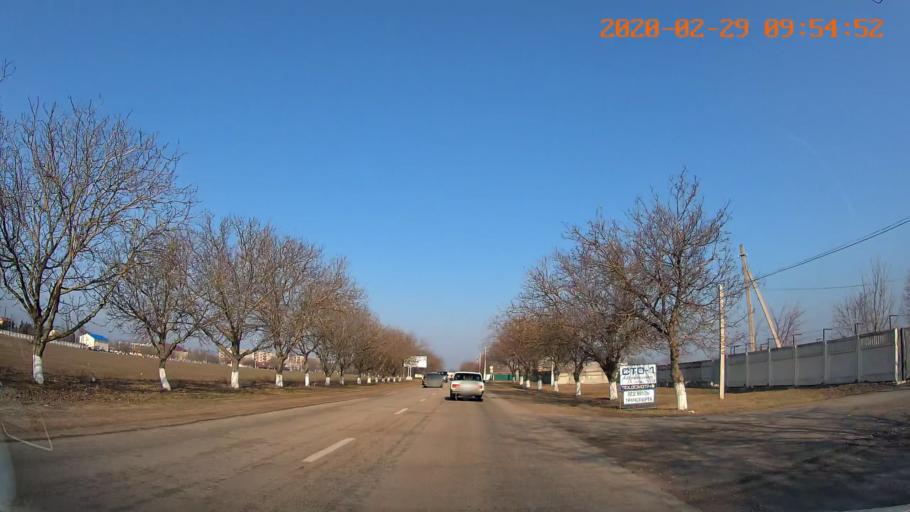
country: MD
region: Telenesti
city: Slobozia
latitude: 46.7316
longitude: 29.7133
